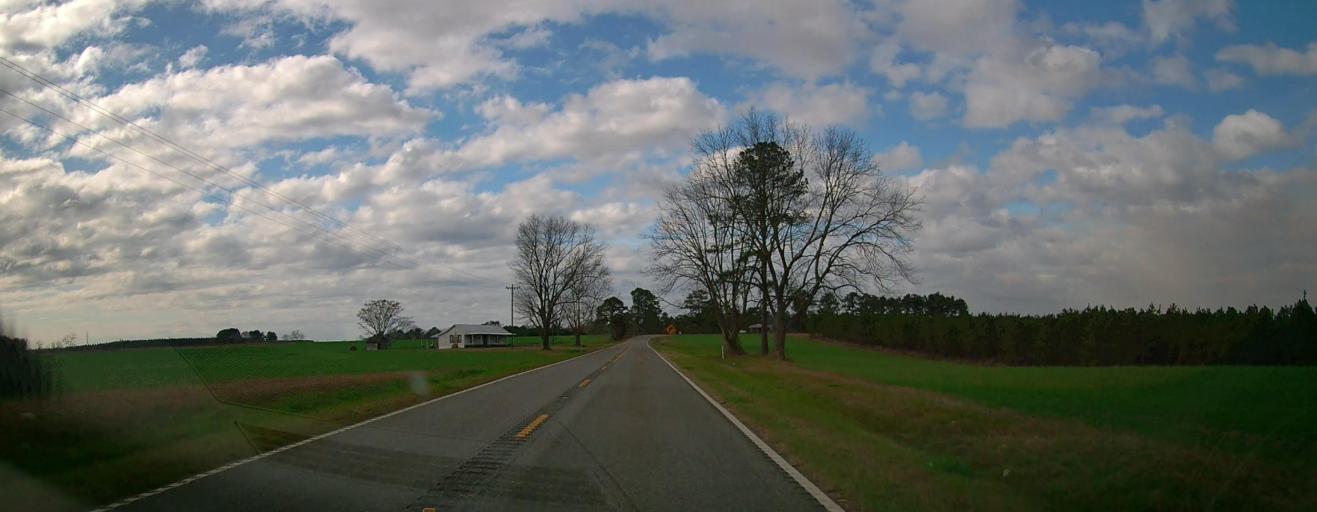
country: US
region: Georgia
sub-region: Marion County
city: Buena Vista
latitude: 32.4409
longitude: -84.4375
